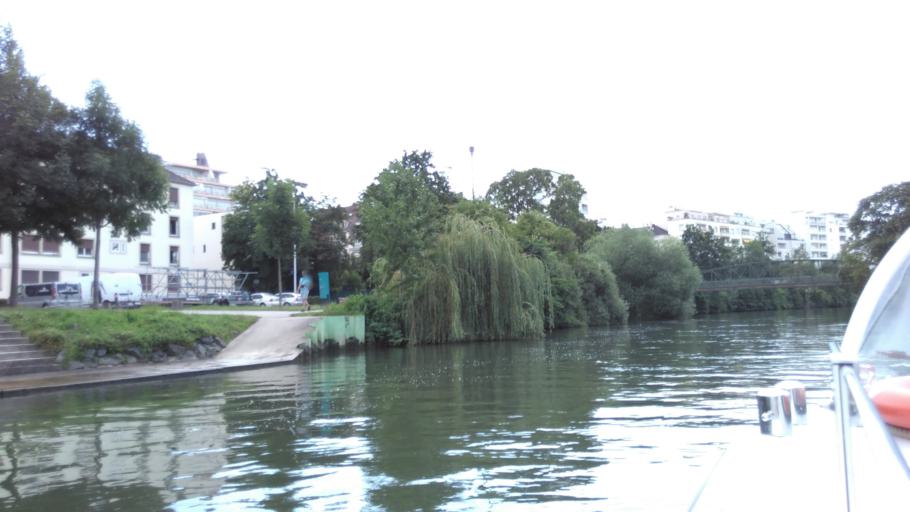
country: FR
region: Alsace
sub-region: Departement du Bas-Rhin
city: Schiltigheim
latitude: 48.5937
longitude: 7.7668
